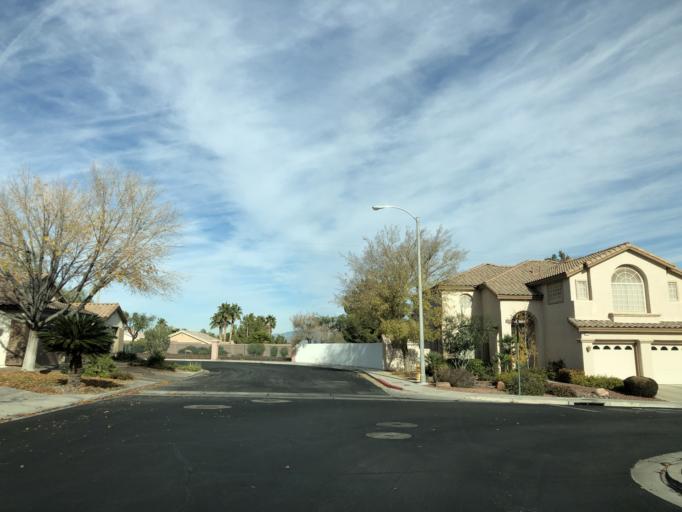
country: US
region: Nevada
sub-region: Clark County
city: Whitney
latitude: 36.0196
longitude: -115.0718
